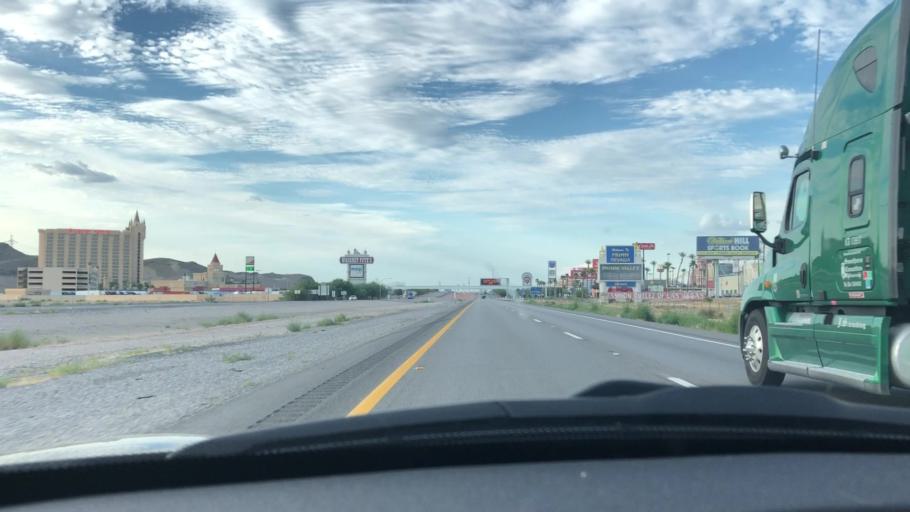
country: US
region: Nevada
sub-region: Clark County
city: Sandy Valley
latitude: 35.6050
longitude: -115.3921
